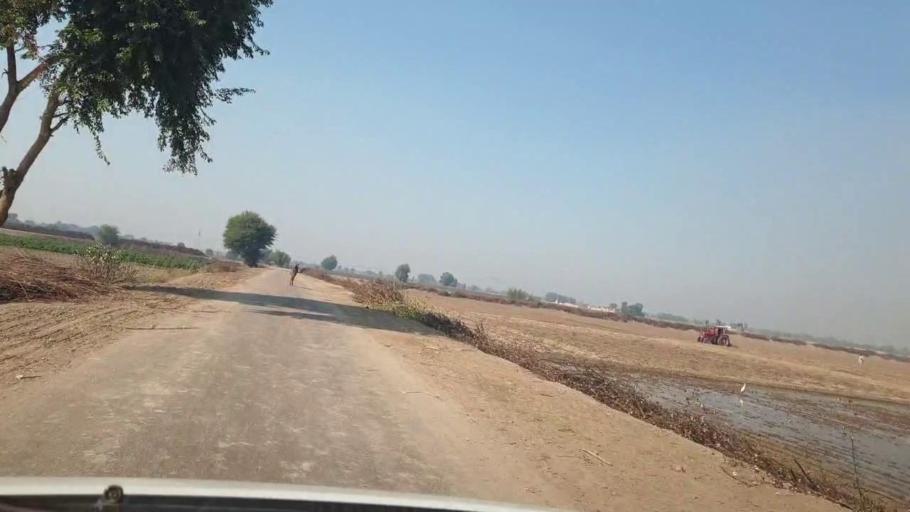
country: PK
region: Sindh
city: Bhan
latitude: 26.6116
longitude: 67.7622
